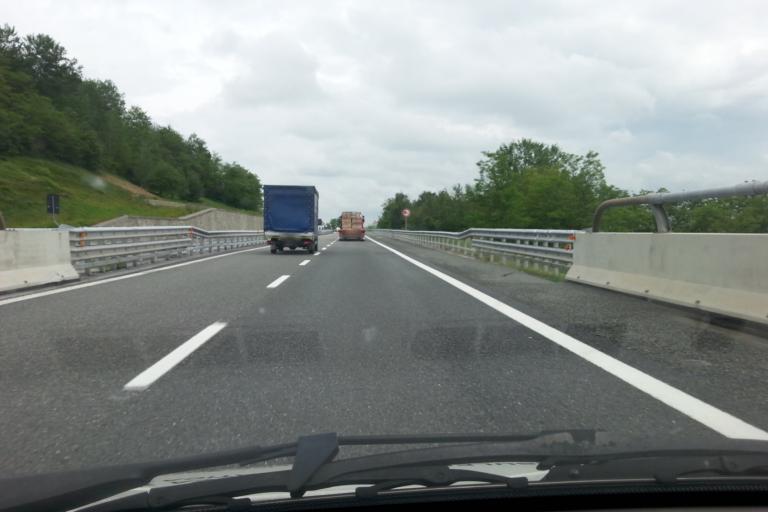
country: IT
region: Piedmont
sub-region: Provincia di Cuneo
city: Bastia Mondovi
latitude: 44.4204
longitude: 7.8902
